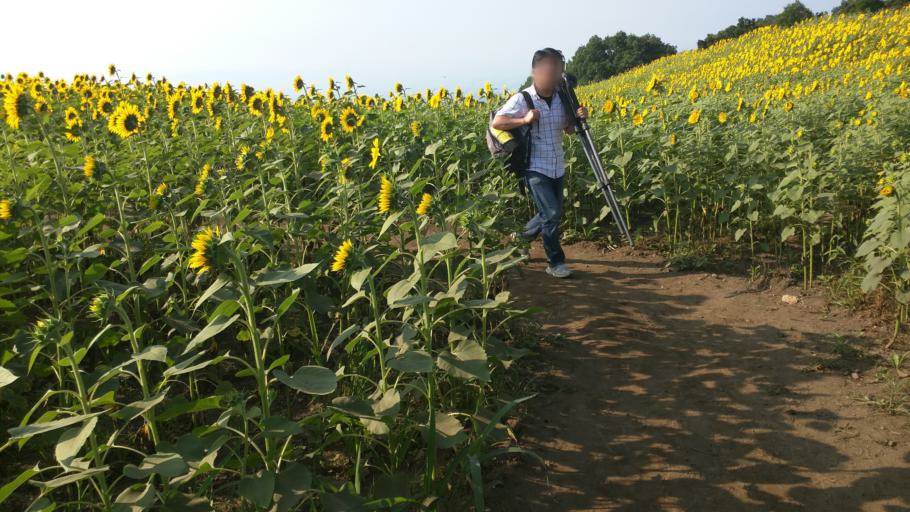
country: JP
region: Fukushima
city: Kitakata
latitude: 37.7495
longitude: 139.8659
